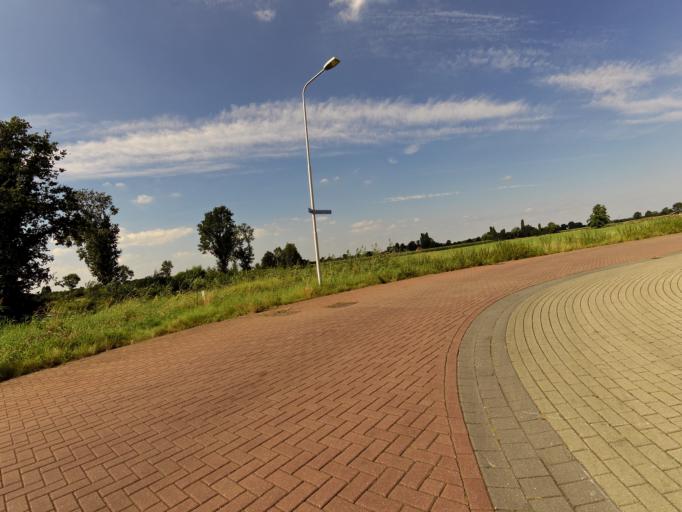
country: NL
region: Gelderland
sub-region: Gemeente Montferland
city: s-Heerenberg
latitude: 51.9203
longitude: 6.1839
